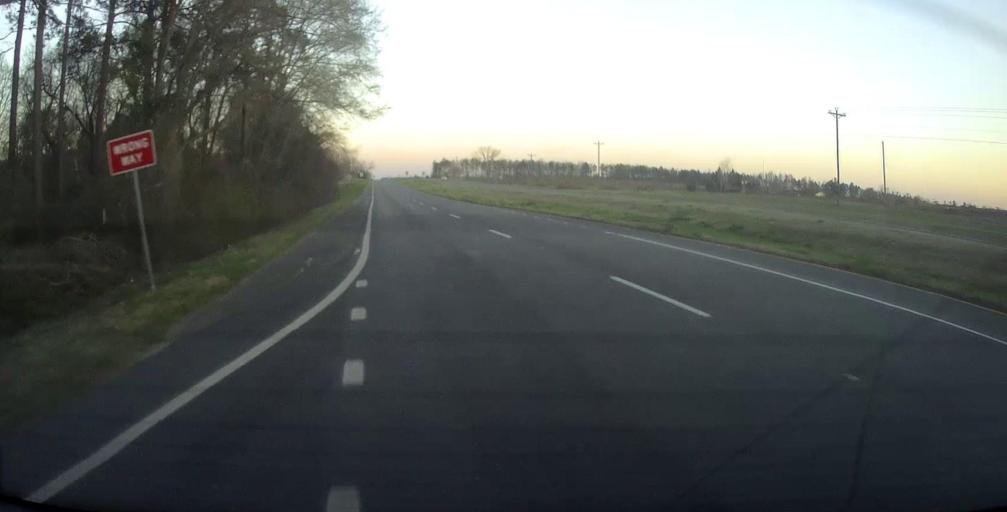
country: US
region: Georgia
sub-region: Dodge County
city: Eastman
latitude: 32.1614
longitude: -83.1496
